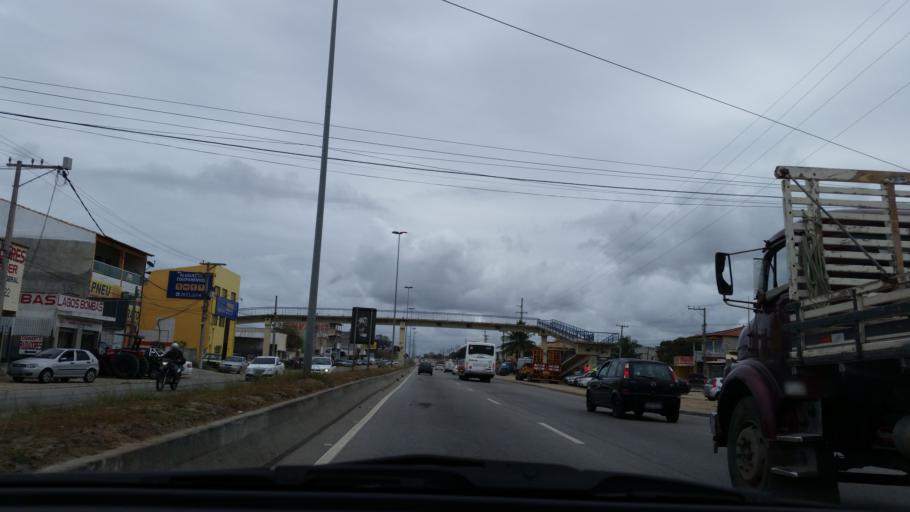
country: BR
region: Rio de Janeiro
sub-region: Sao Pedro Da Aldeia
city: Sao Pedro da Aldeia
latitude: -22.8410
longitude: -42.0723
